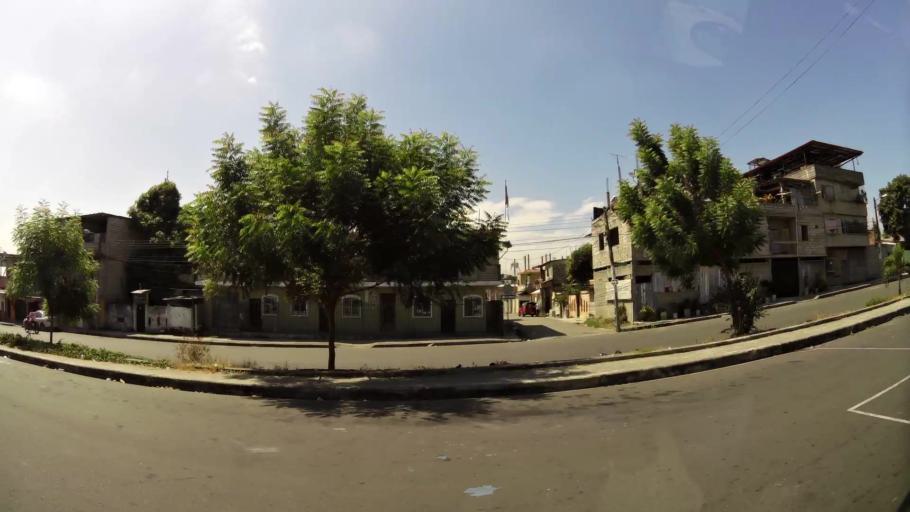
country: EC
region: Guayas
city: Guayaquil
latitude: -2.1267
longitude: -79.9230
